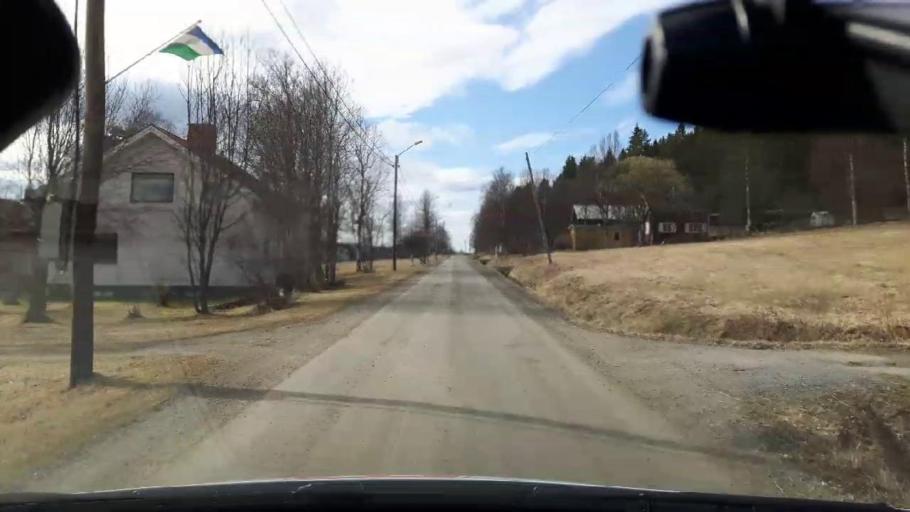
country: SE
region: Jaemtland
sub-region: Bergs Kommun
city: Hoverberg
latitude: 62.7147
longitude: 14.6856
